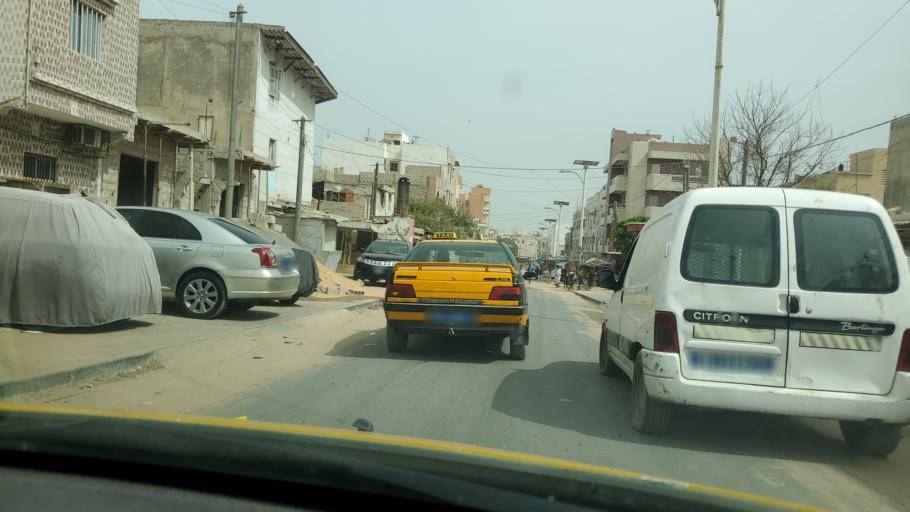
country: SN
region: Dakar
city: Pikine
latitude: 14.7721
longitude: -17.3943
